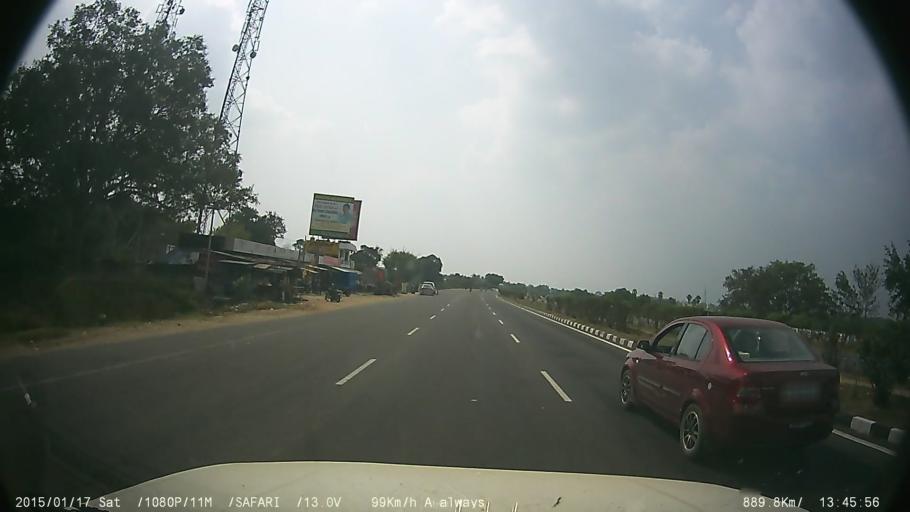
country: IN
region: Tamil Nadu
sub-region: Vellore
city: Vellore
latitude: 12.9157
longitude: 79.0880
